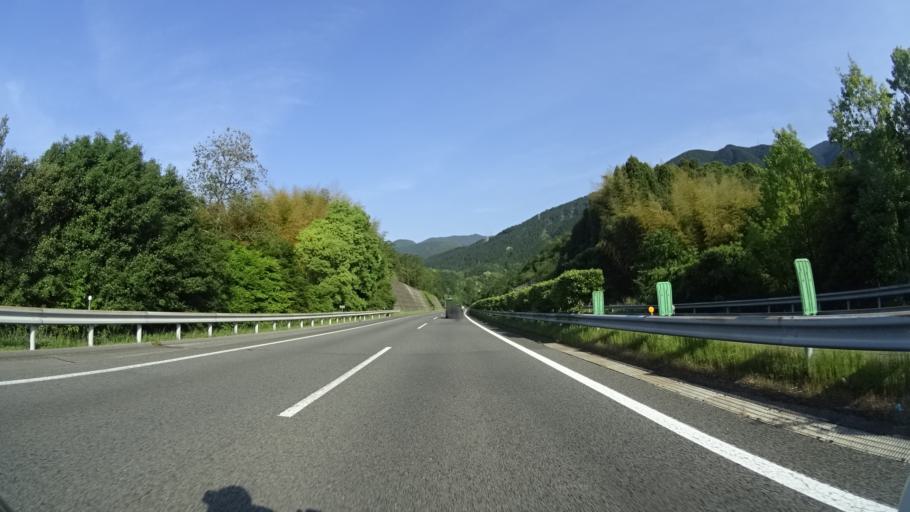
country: JP
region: Ehime
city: Saijo
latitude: 33.9110
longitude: 133.2468
